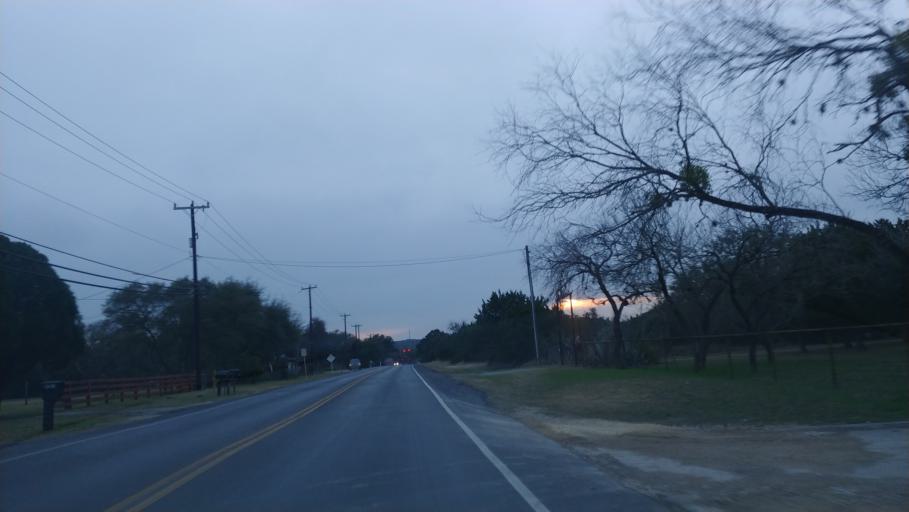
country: US
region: Texas
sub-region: Bexar County
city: Helotes
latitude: 29.5834
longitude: -98.6888
